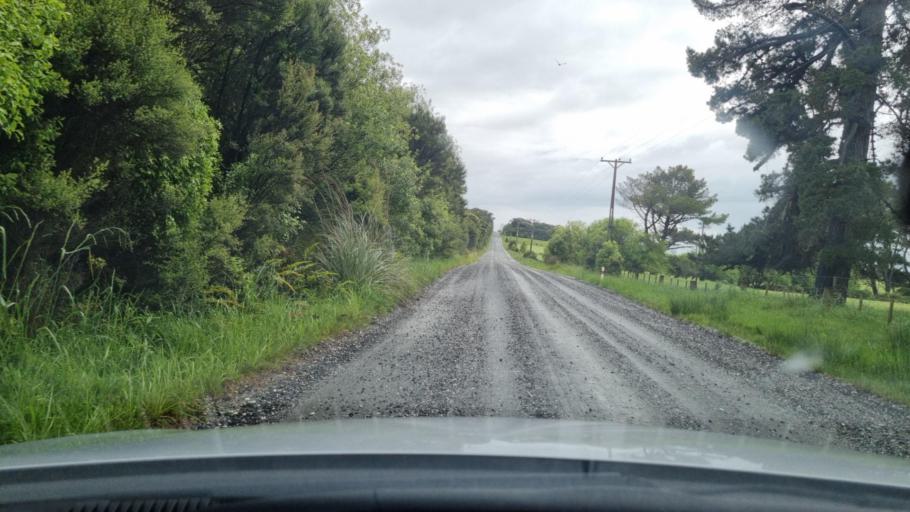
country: NZ
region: Southland
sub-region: Invercargill City
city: Bluff
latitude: -46.5330
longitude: 168.2671
